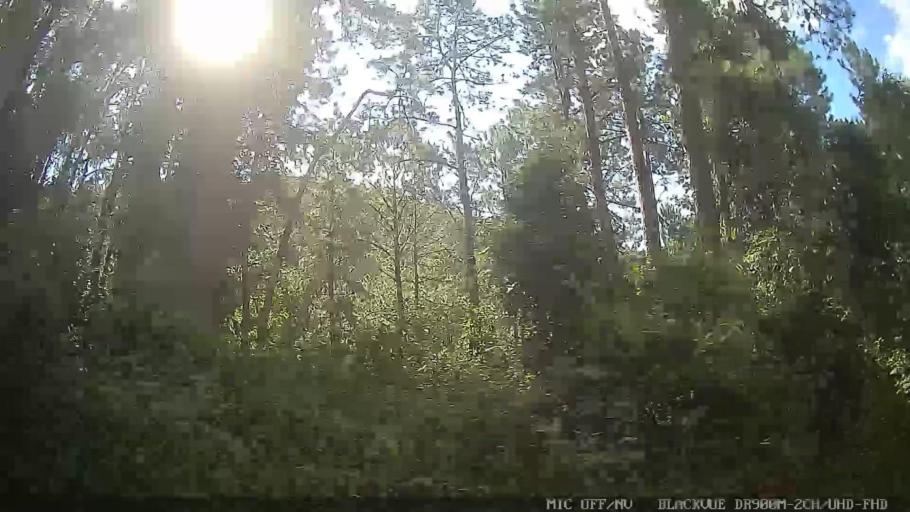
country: BR
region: Sao Paulo
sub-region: Bom Jesus Dos Perdoes
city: Bom Jesus dos Perdoes
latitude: -23.1657
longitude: -46.5128
